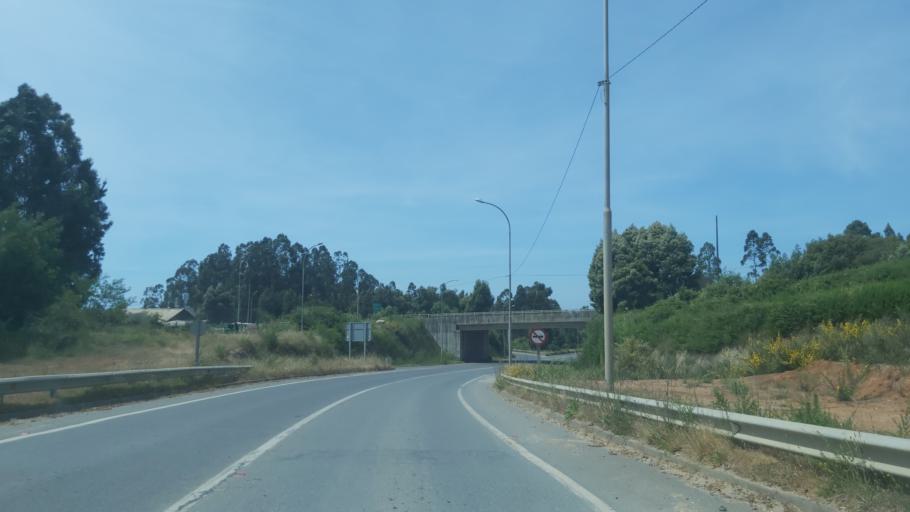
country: CL
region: Maule
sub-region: Provincia de Talca
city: Constitucion
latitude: -35.3666
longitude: -72.4020
